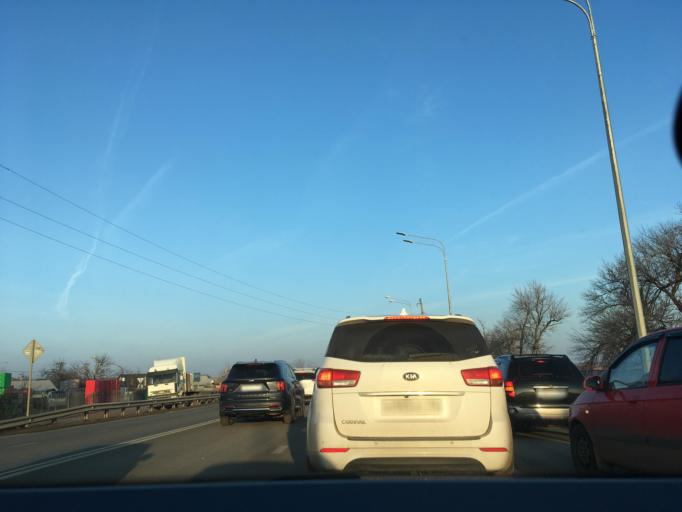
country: RU
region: Krasnodarskiy
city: Krasnodar
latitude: 45.1291
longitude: 39.0158
